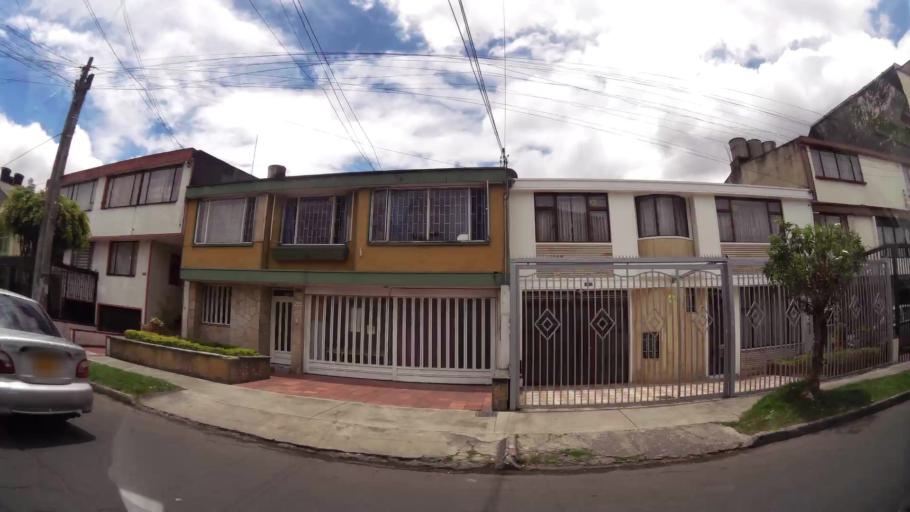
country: CO
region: Bogota D.C.
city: Bogota
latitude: 4.6707
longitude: -74.1032
